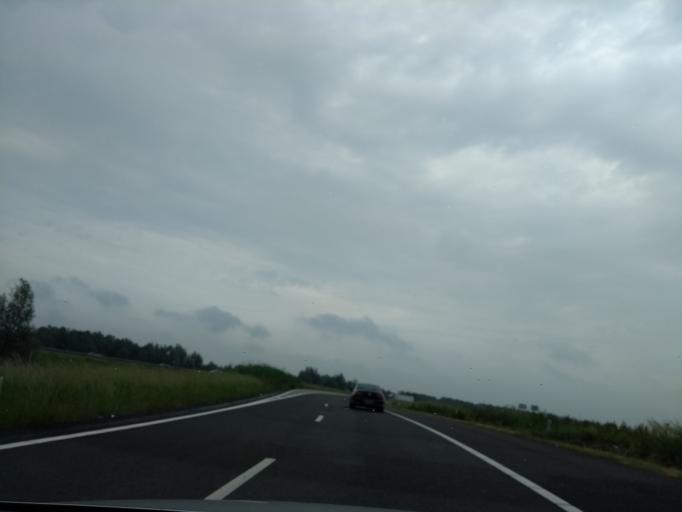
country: NL
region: Utrecht
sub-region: Gemeente Bunschoten
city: Spakenburg
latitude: 52.3132
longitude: 5.3286
